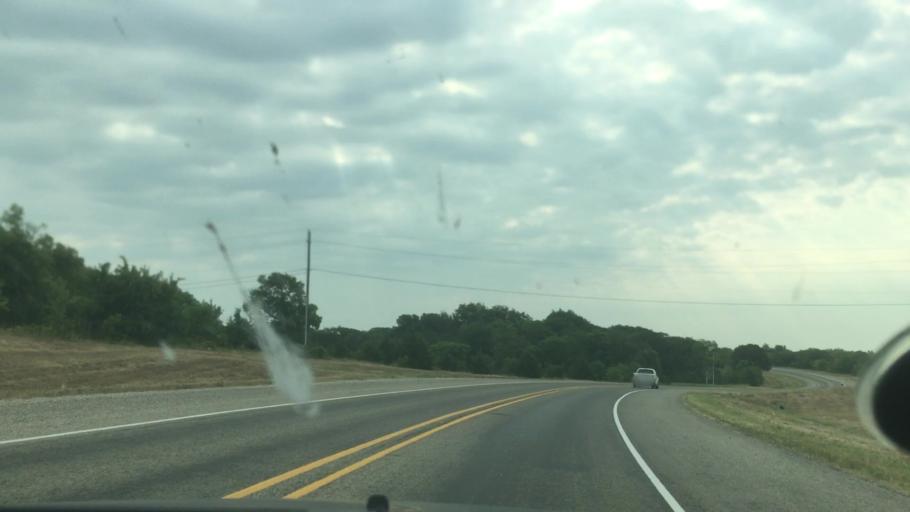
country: US
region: Texas
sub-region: Grayson County
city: Pottsboro
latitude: 33.8015
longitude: -96.6533
